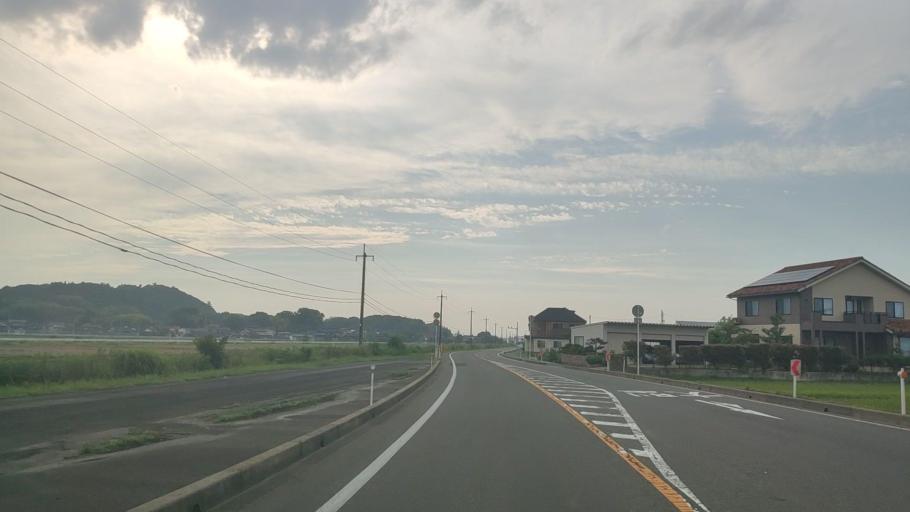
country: JP
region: Tottori
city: Kurayoshi
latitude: 35.4766
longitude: 133.8200
